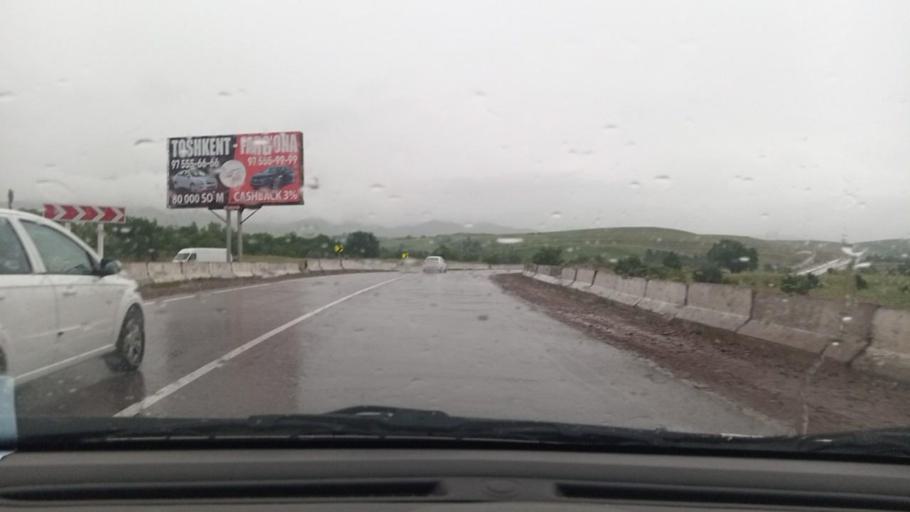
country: UZ
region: Toshkent
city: Angren
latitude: 41.0495
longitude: 70.1587
